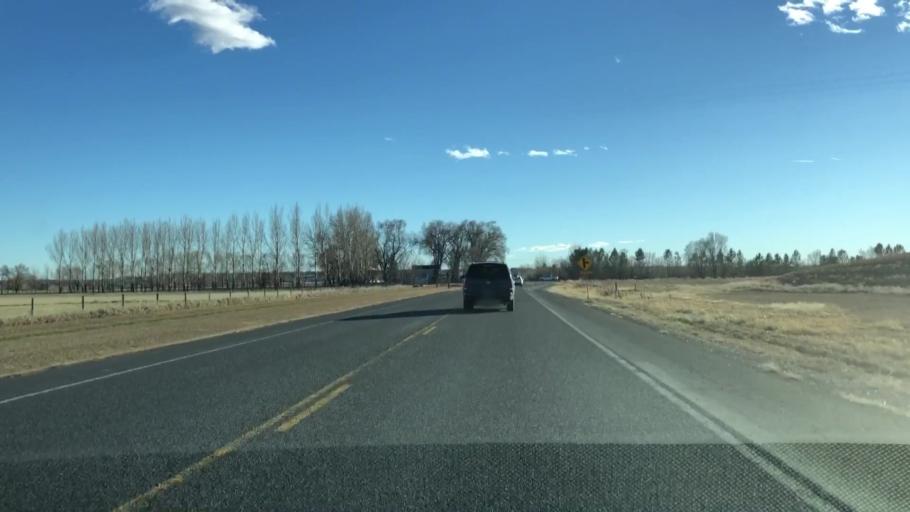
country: US
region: Colorado
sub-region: Weld County
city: Windsor
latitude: 40.5108
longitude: -104.9818
